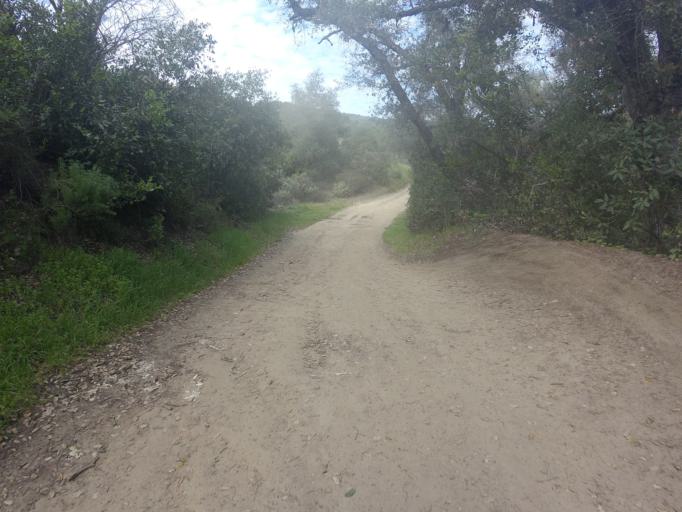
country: US
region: California
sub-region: Orange County
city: Aliso Viejo
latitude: 33.5783
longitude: -117.7476
